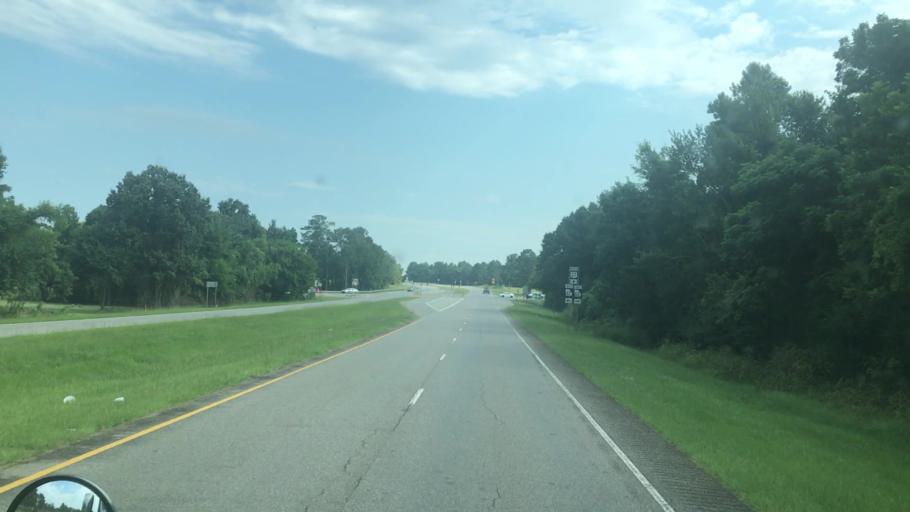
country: US
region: Georgia
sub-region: Early County
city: Blakely
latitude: 31.3786
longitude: -84.9213
